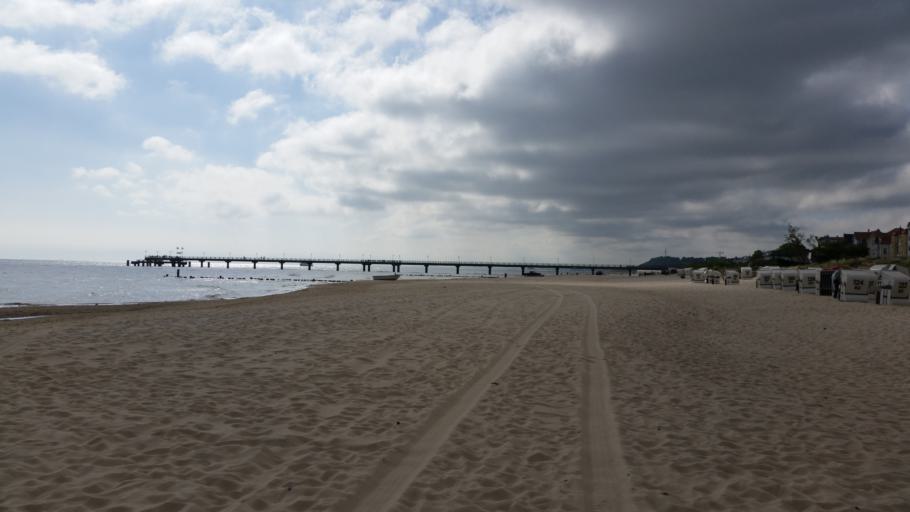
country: DE
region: Mecklenburg-Vorpommern
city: Seebad Bansin
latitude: 53.9773
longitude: 14.1405
